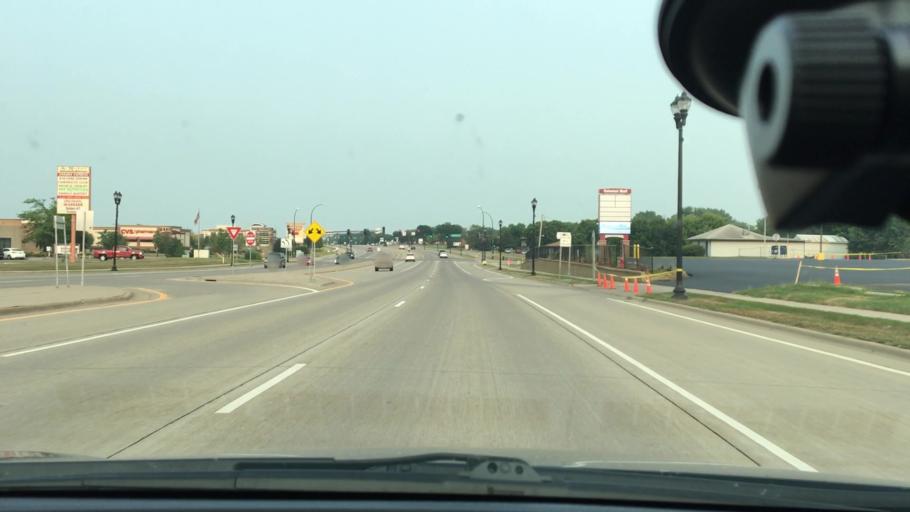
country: US
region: Minnesota
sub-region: Wright County
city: Saint Michael
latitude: 45.2099
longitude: -93.6564
